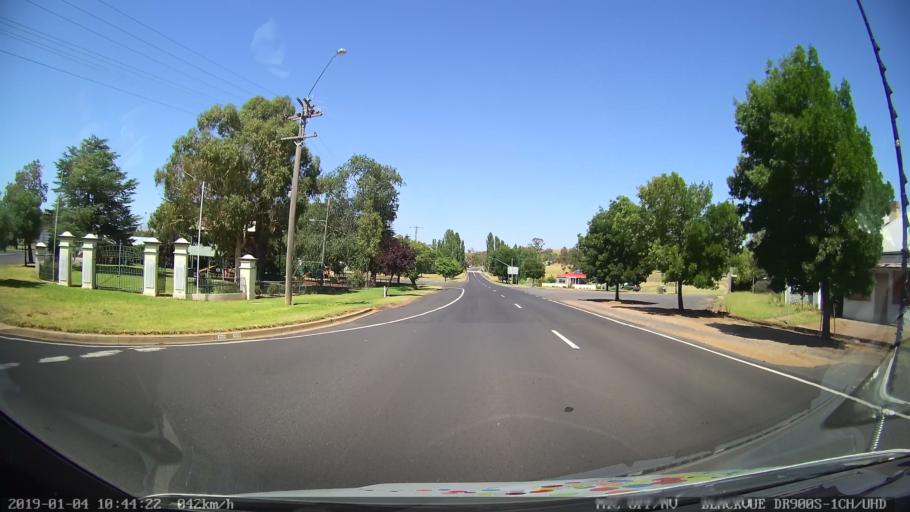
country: AU
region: New South Wales
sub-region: Cabonne
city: Molong
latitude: -33.2874
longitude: 148.7374
